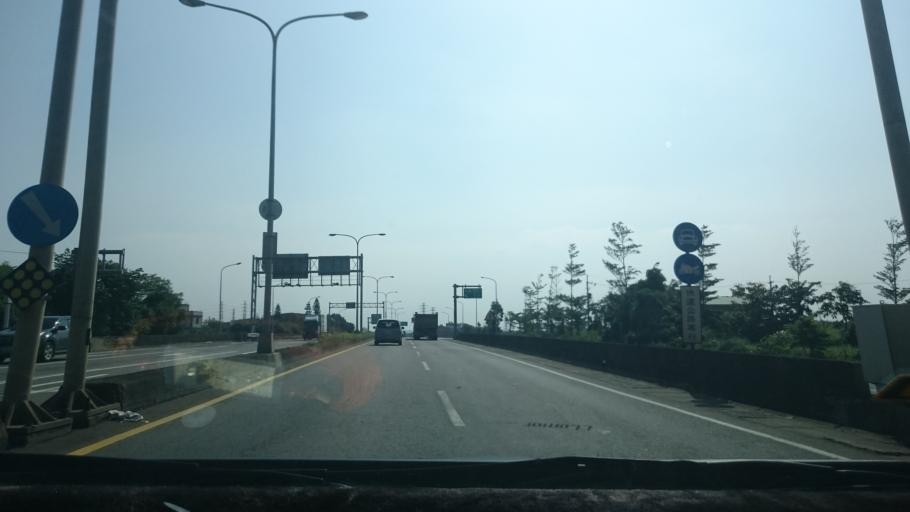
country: TW
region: Taiwan
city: Taoyuan City
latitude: 24.9876
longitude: 121.1230
